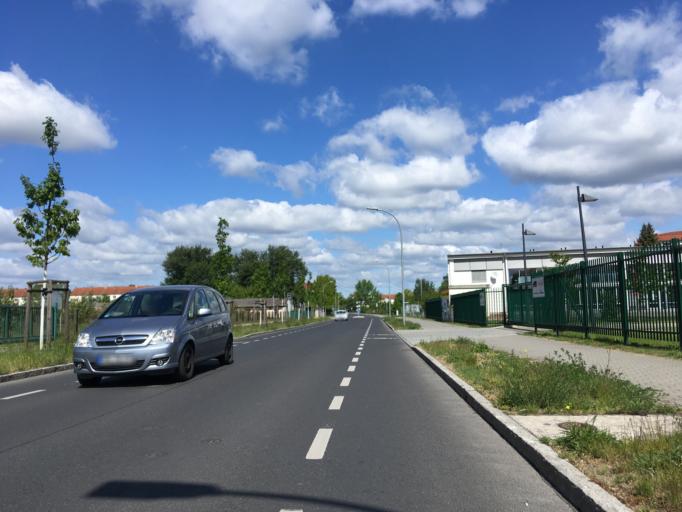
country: DE
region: Brandenburg
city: Oranienburg
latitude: 52.7489
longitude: 13.2509
